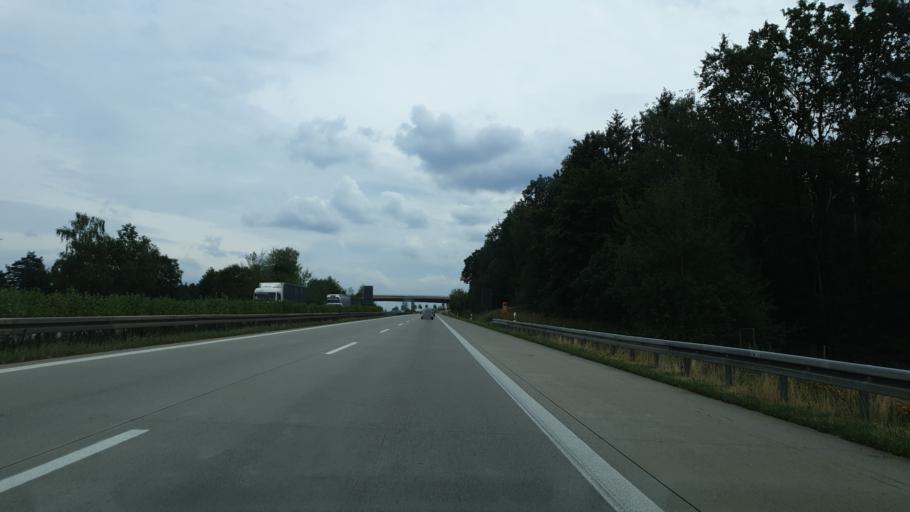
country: DE
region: Saxony
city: Wildenfels
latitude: 50.6834
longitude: 12.6278
